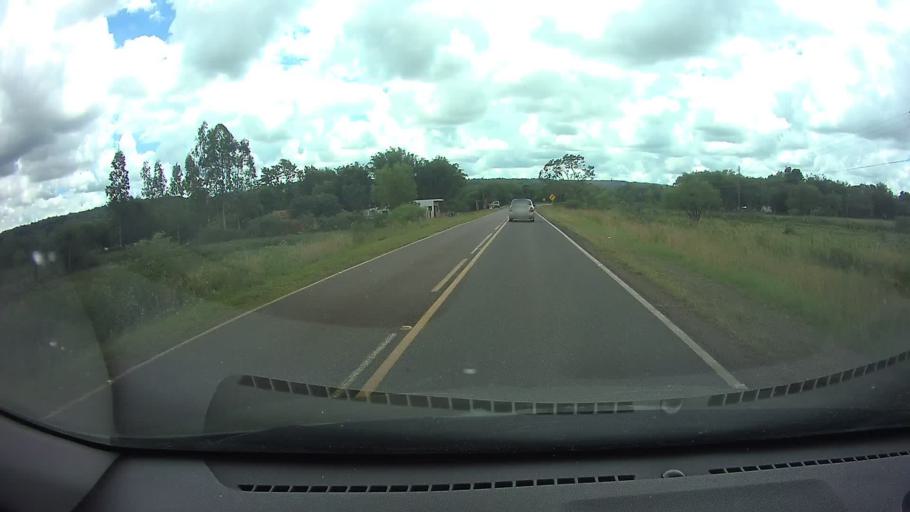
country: PY
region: Paraguari
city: Ybycui
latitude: -25.8999
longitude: -56.9723
